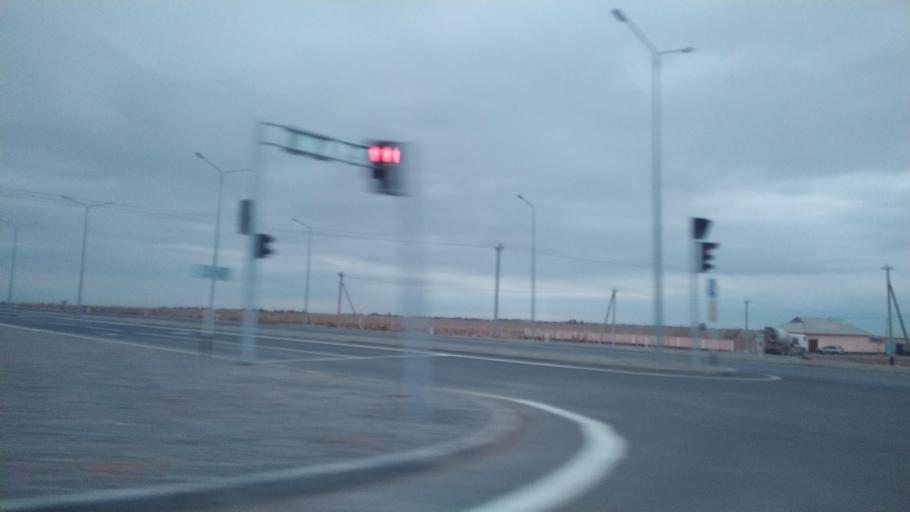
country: KZ
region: Ongtustik Qazaqstan
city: Turkestan
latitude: 43.2763
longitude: 68.4191
